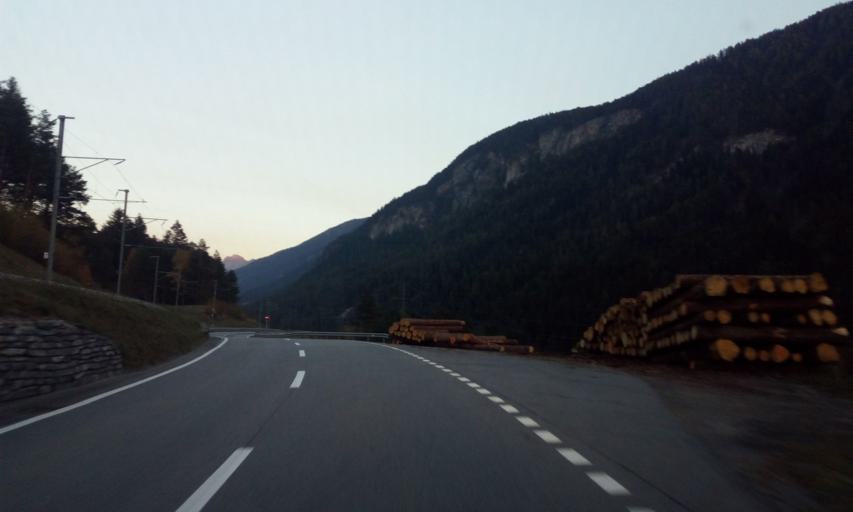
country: CH
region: Grisons
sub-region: Albula District
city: Tiefencastel
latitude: 46.6610
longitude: 9.5876
